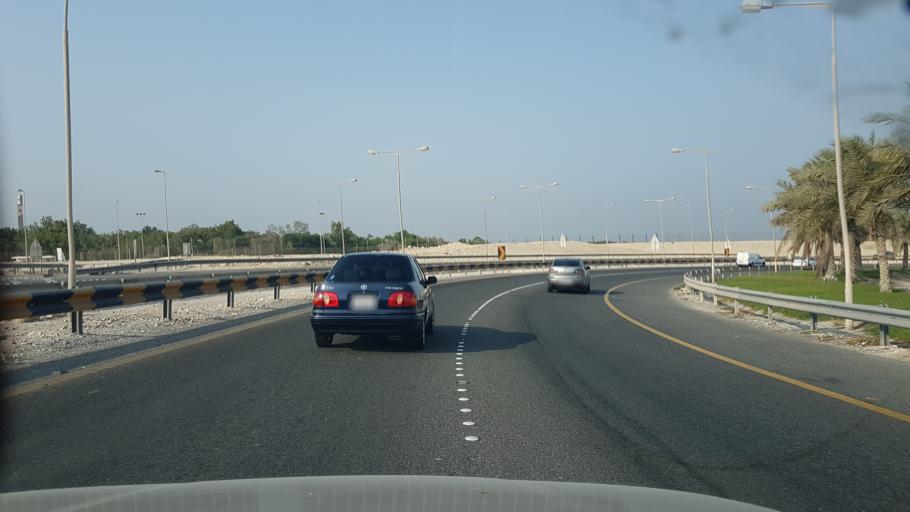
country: BH
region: Central Governorate
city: Dar Kulayb
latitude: 26.0565
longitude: 50.5179
